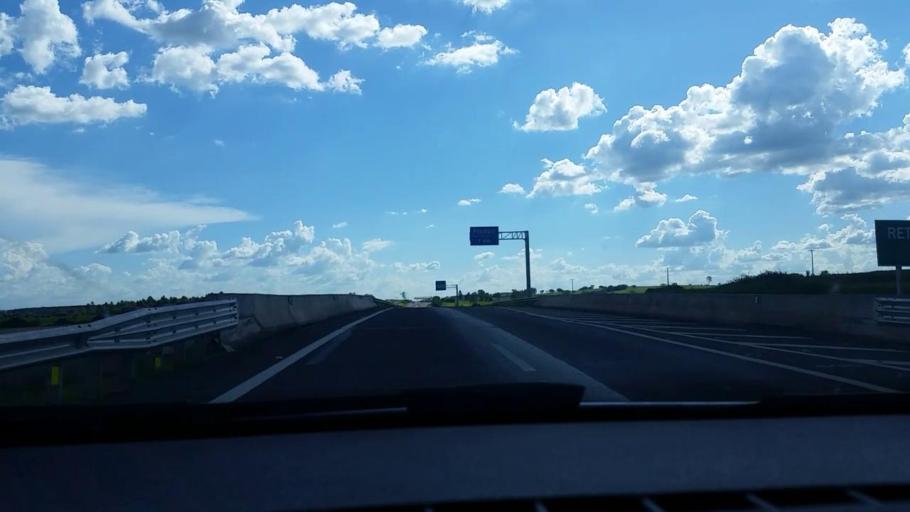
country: BR
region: Sao Paulo
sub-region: Bauru
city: Bauru
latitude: -22.4459
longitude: -49.1590
